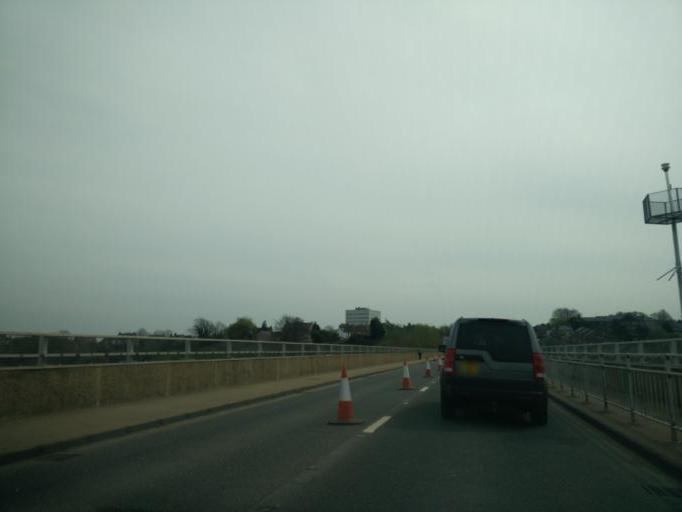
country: GB
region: England
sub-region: County Durham
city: Bishop Auckland
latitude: 54.6676
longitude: -1.6821
